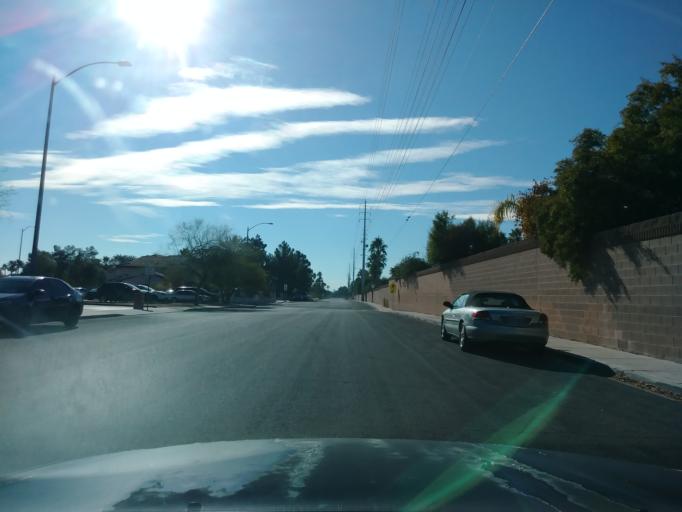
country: US
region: Nevada
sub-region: Clark County
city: Spring Valley
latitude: 36.1504
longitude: -115.2773
